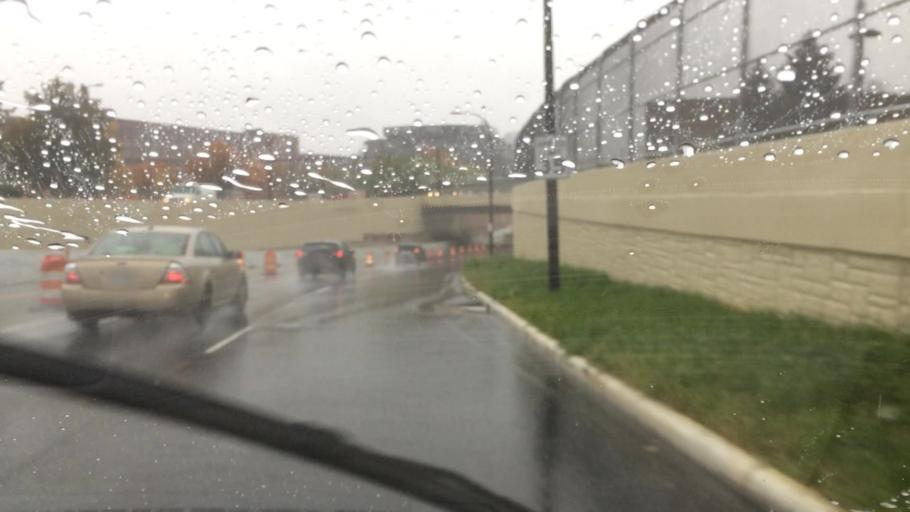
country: US
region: Ohio
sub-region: Summit County
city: Akron
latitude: 41.0680
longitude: -81.5261
